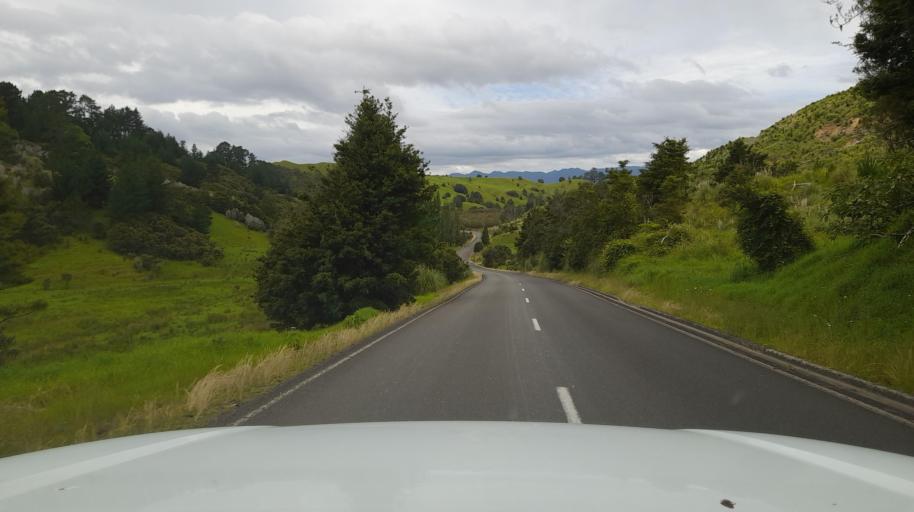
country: NZ
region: Northland
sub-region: Far North District
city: Kaitaia
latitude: -35.3582
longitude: 173.4675
